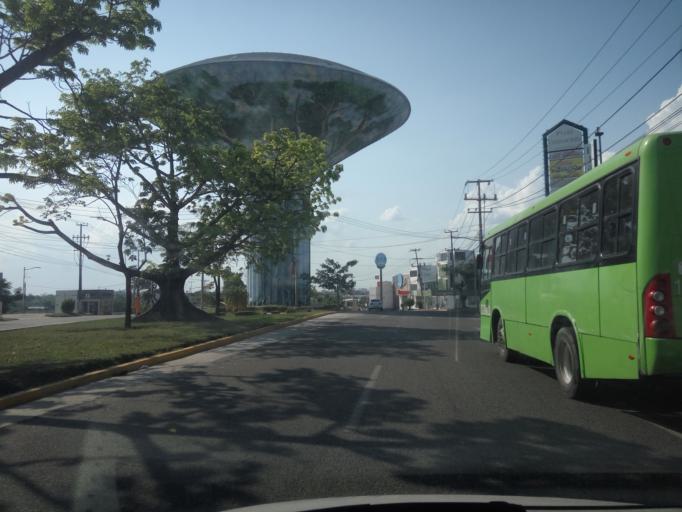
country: MX
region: Tabasco
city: Villahermosa
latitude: 17.9930
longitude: -92.9461
